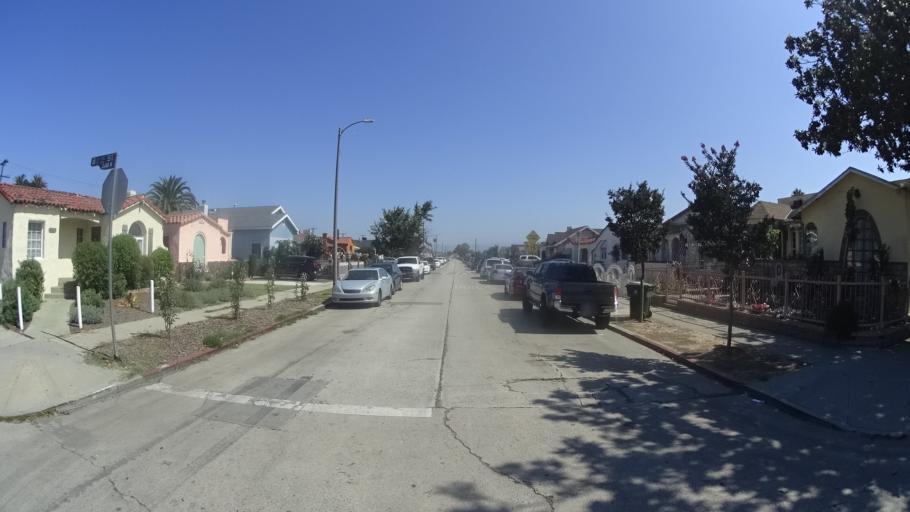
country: US
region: California
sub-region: Los Angeles County
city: View Park-Windsor Hills
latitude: 33.9781
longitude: -118.3187
